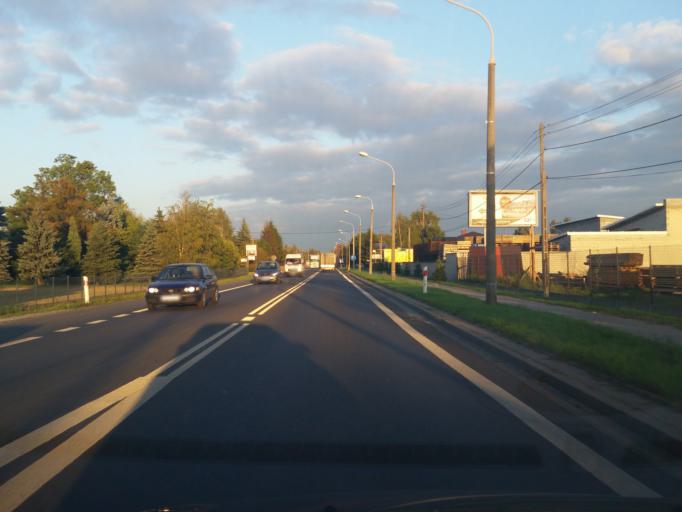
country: PL
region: Masovian Voivodeship
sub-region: Powiat warszawski zachodni
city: Ozarow Mazowiecki
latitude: 52.2108
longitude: 20.7803
